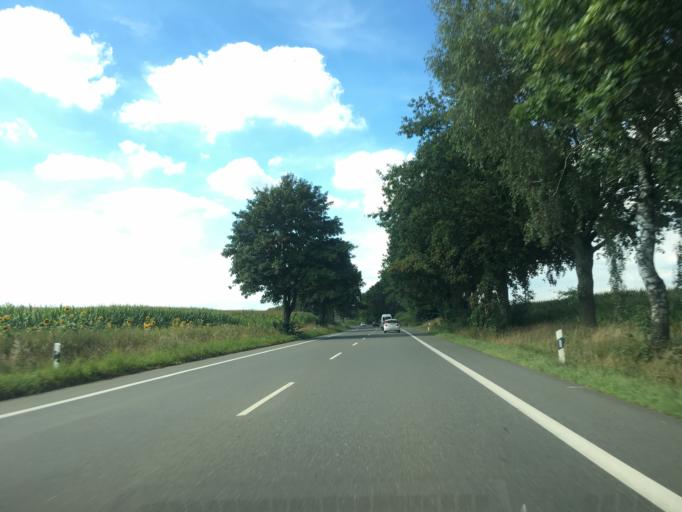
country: DE
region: North Rhine-Westphalia
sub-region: Regierungsbezirk Detmold
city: Dorentrup
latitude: 51.9931
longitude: 8.9849
